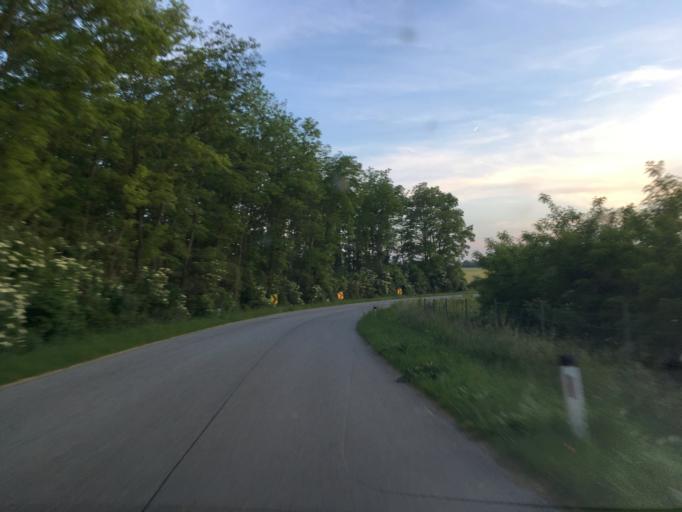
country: AT
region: Lower Austria
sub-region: Politischer Bezirk Mistelbach
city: Herrnbaumgarten
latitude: 48.7134
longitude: 16.6671
